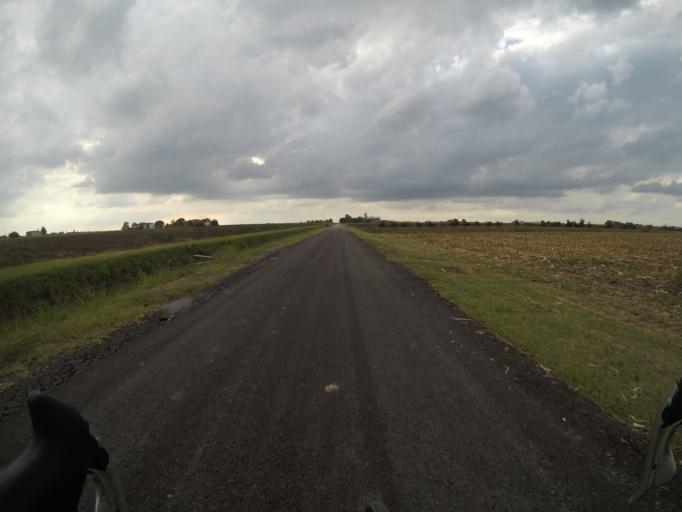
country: IT
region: Veneto
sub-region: Provincia di Rovigo
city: Polesella
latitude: 44.9658
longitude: 11.7331
